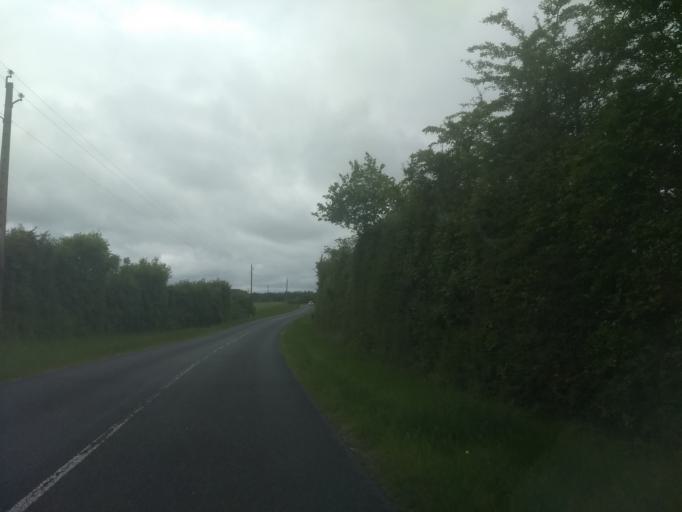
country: FR
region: Centre
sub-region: Departement d'Eure-et-Loir
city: La Loupe
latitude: 48.5085
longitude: 1.0439
